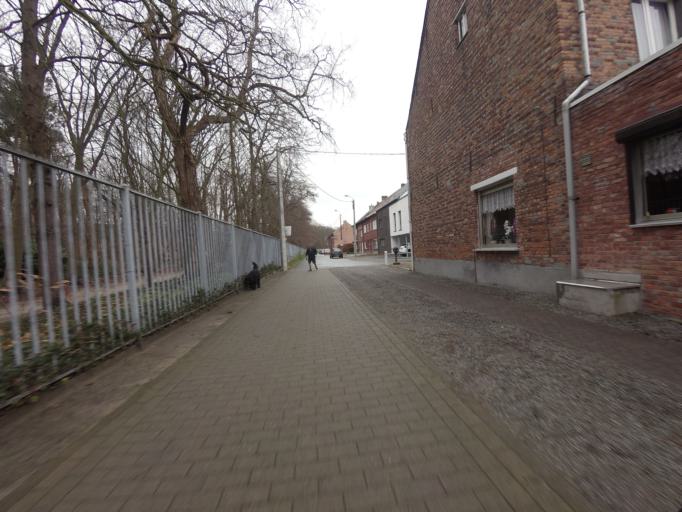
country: BE
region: Flanders
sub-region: Provincie Antwerpen
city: Sint-Katelijne-Waver
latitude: 51.0411
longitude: 4.5104
